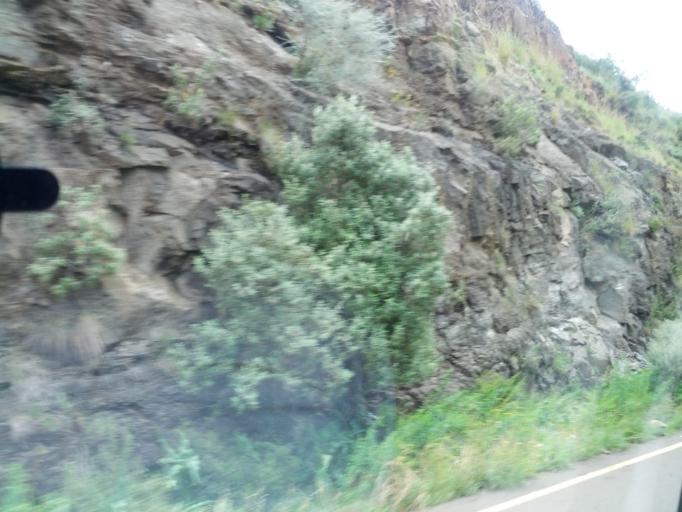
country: LS
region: Butha-Buthe
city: Butha-Buthe
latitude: -29.0542
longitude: 28.3453
